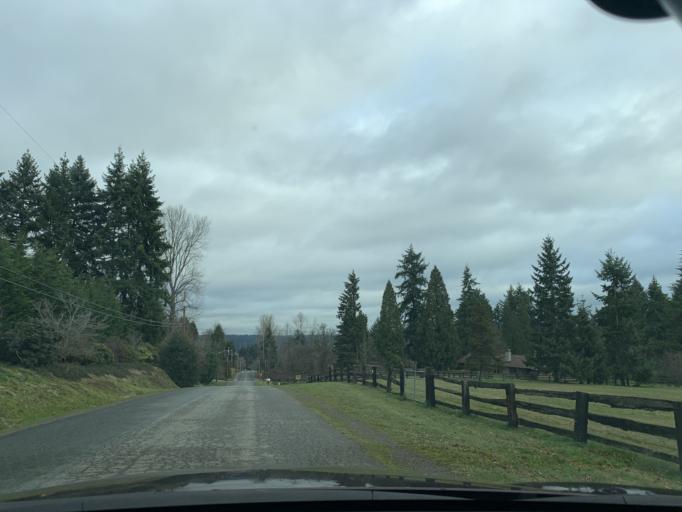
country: US
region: Washington
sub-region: King County
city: Kingsgate
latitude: 47.7341
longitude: -122.1637
